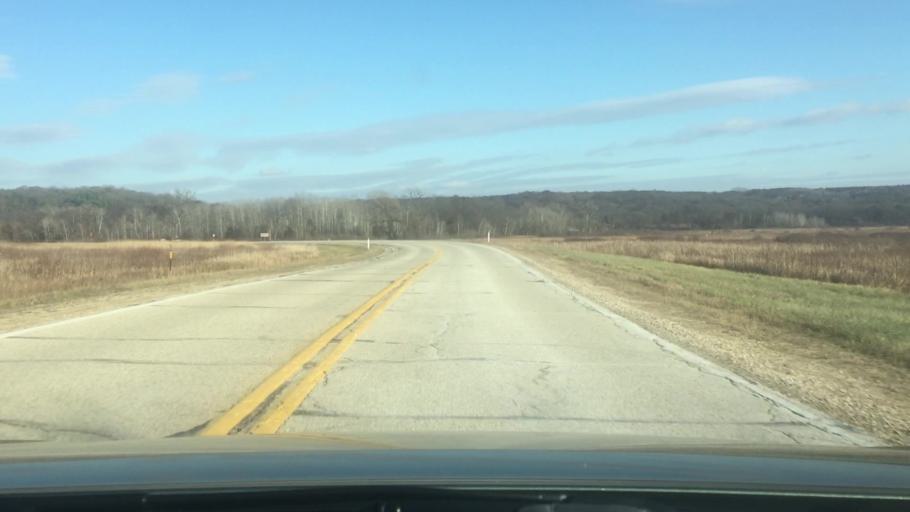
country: US
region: Wisconsin
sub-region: Waukesha County
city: Eagle
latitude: 42.9343
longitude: -88.4788
